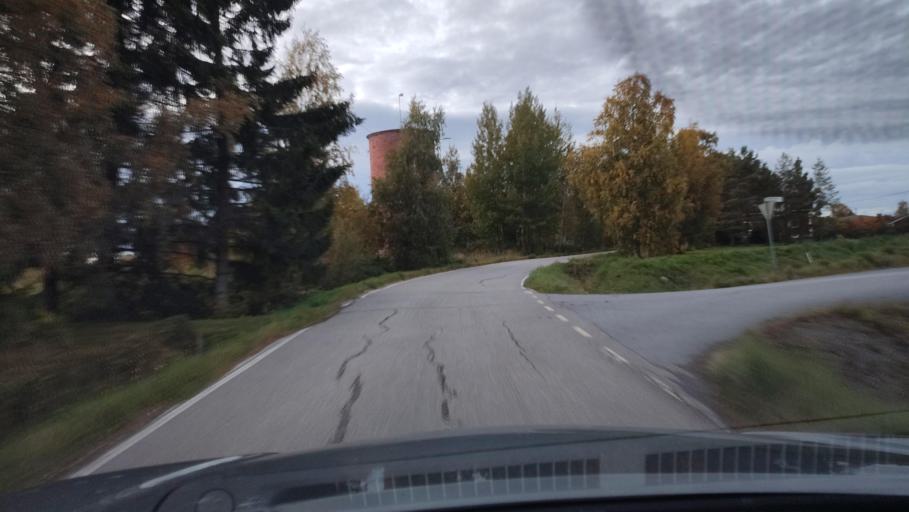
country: FI
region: Ostrobothnia
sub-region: Sydosterbotten
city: Kristinestad
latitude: 62.2559
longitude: 21.5101
